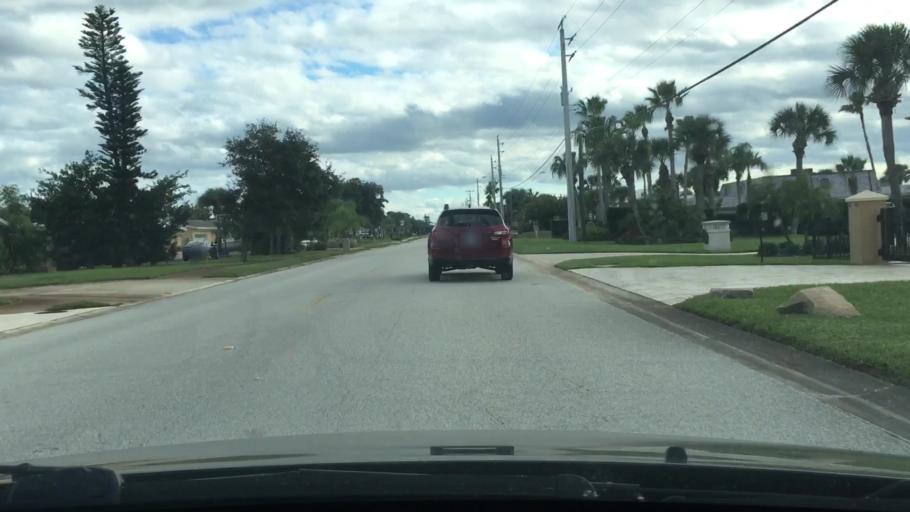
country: US
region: Florida
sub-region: Volusia County
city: Ormond Beach
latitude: 29.2695
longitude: -81.0378
